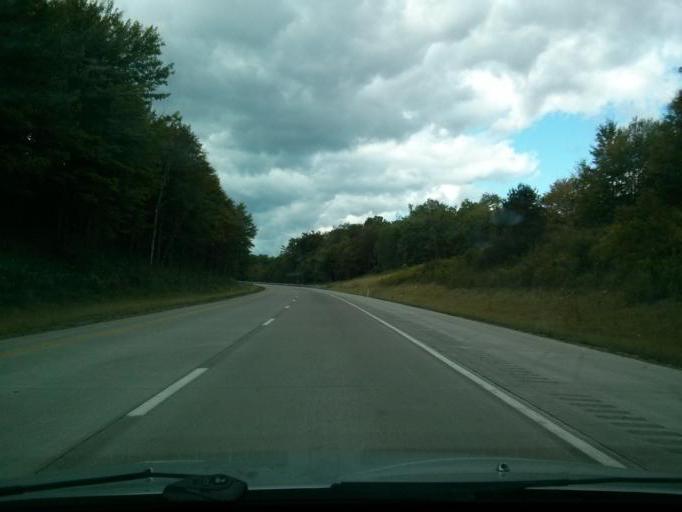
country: US
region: Pennsylvania
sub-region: Jefferson County
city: Falls Creek
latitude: 41.1588
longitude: -78.8292
